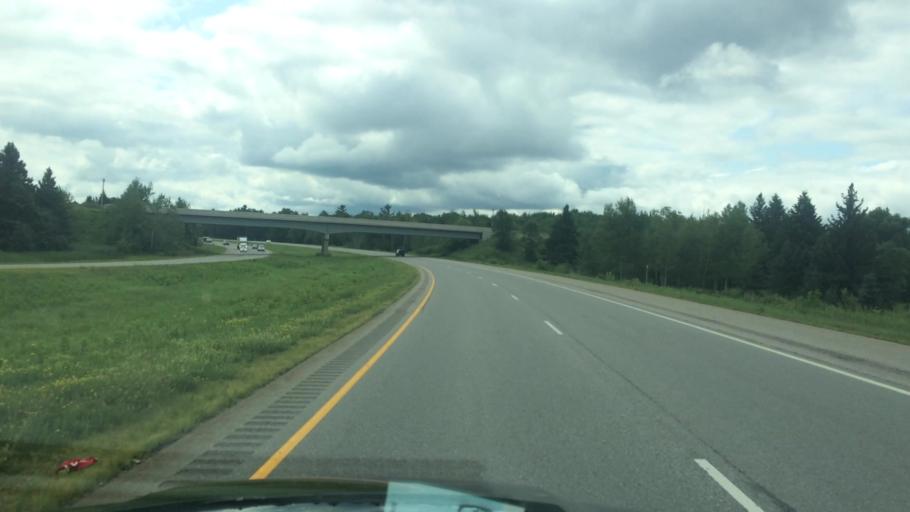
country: US
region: Wisconsin
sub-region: Marathon County
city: Mosinee
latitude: 44.7308
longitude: -89.6797
